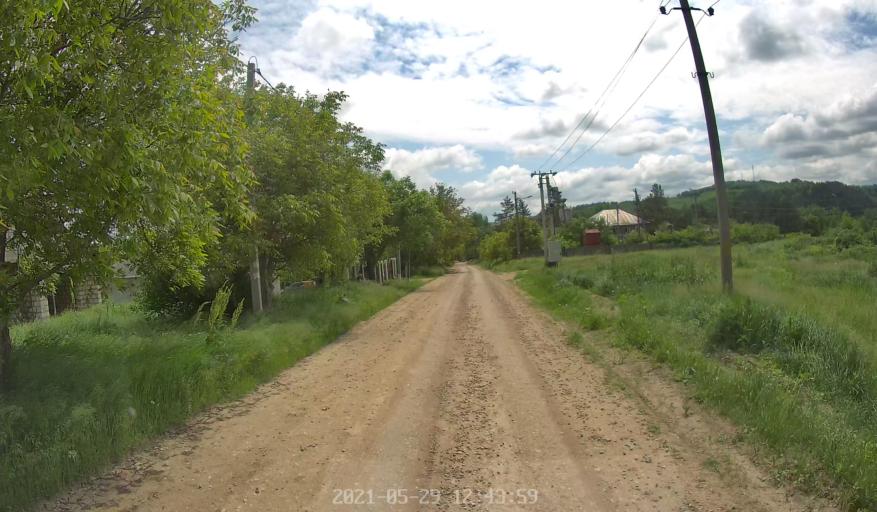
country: MD
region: Hincesti
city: Hincesti
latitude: 46.8721
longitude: 28.6377
